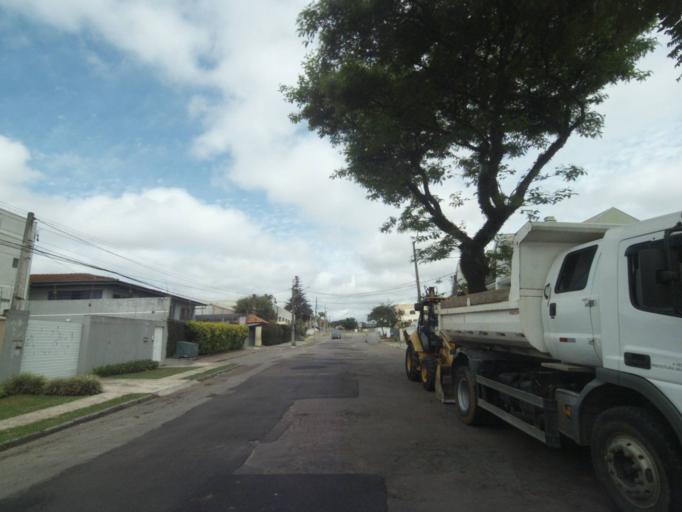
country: BR
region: Parana
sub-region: Pinhais
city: Pinhais
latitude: -25.4317
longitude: -49.2279
